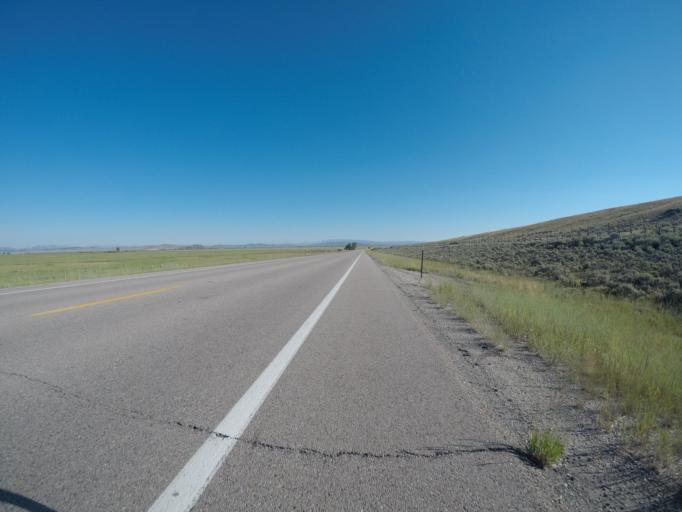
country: US
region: Wyoming
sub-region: Sublette County
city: Pinedale
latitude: 42.9480
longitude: -110.0851
